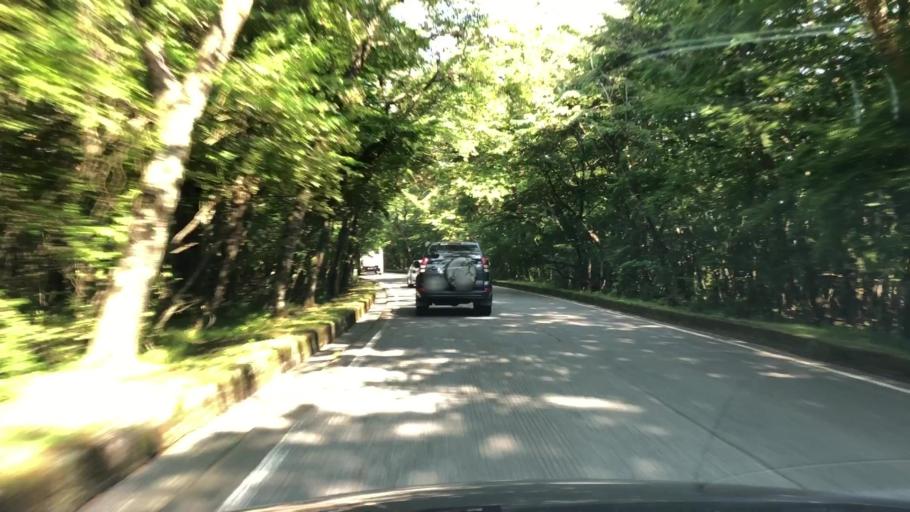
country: JP
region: Shizuoka
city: Gotemba
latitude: 35.3301
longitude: 138.8409
